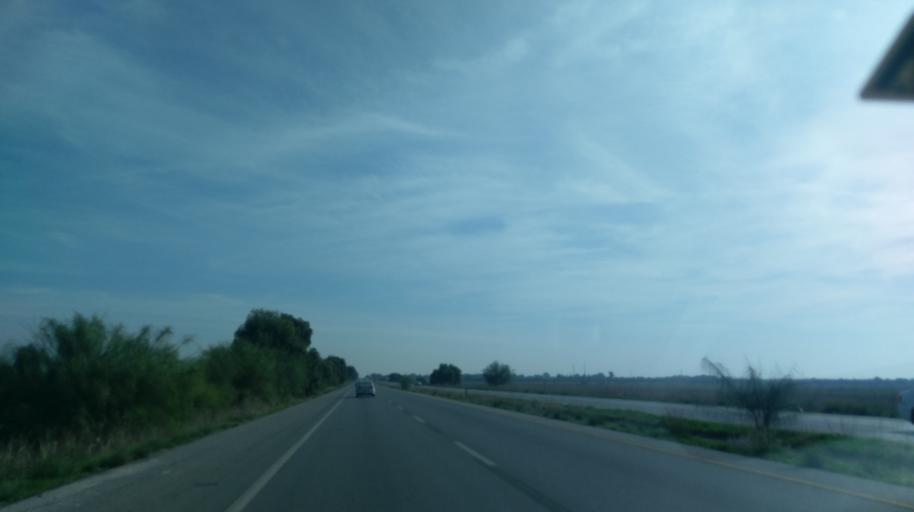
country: CY
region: Larnaka
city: Athienou
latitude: 35.2105
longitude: 33.5657
